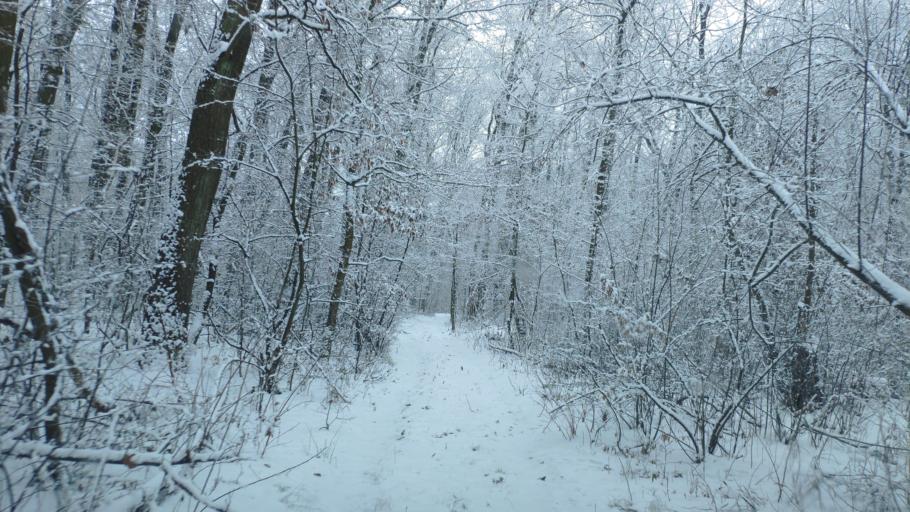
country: SK
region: Kosicky
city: Kosice
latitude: 48.6492
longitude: 21.1794
